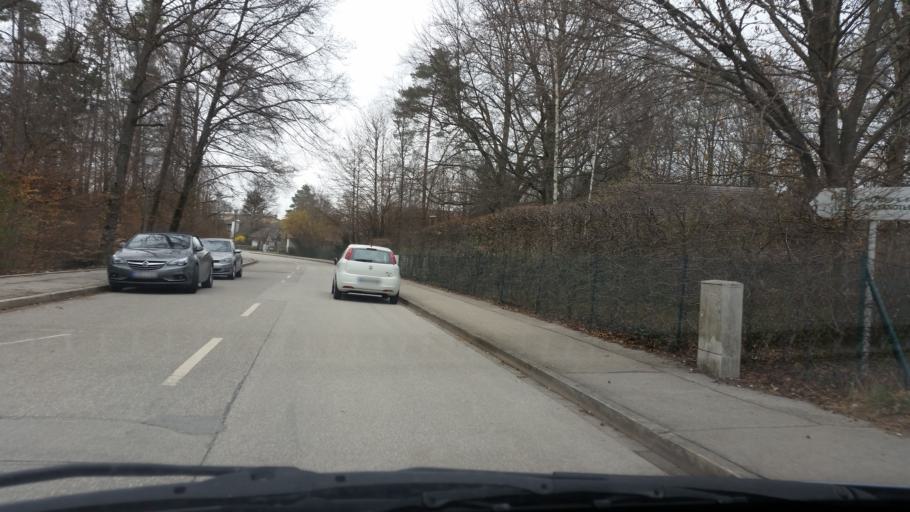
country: DE
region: Bavaria
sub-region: Upper Bavaria
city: Geretsried
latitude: 47.8524
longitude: 11.4847
